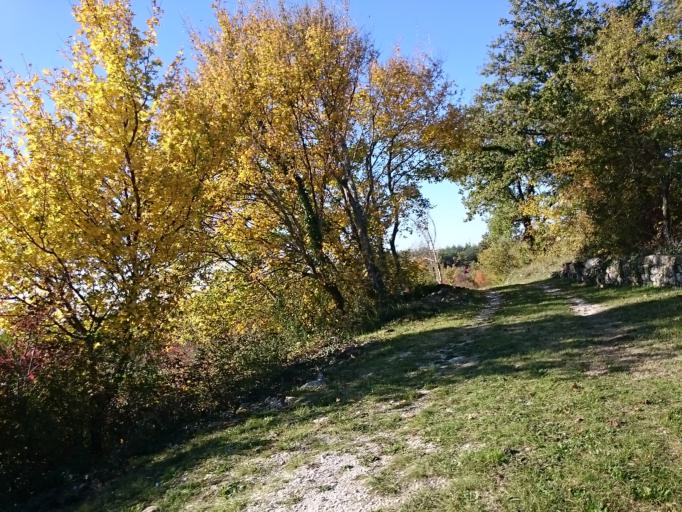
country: HR
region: Istarska
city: Buje
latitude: 45.4322
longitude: 13.7396
